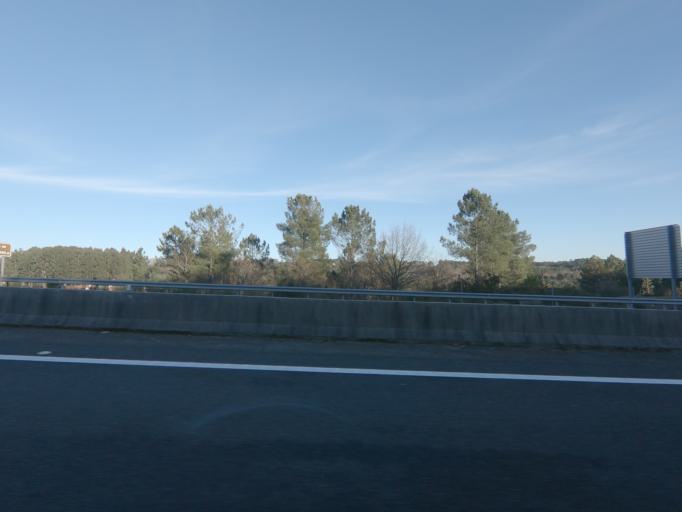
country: ES
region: Galicia
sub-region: Provincia de Ourense
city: Pinor
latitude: 42.5124
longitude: -8.0212
